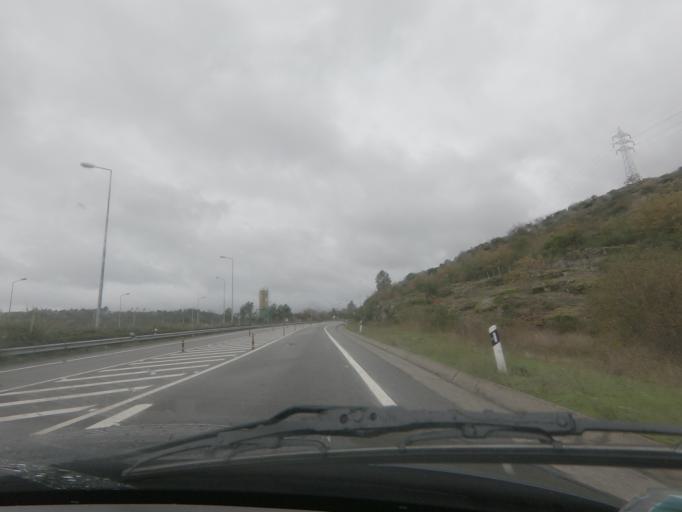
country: PT
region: Vila Real
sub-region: Vila Real
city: Vila Real
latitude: 41.2848
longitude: -7.8147
